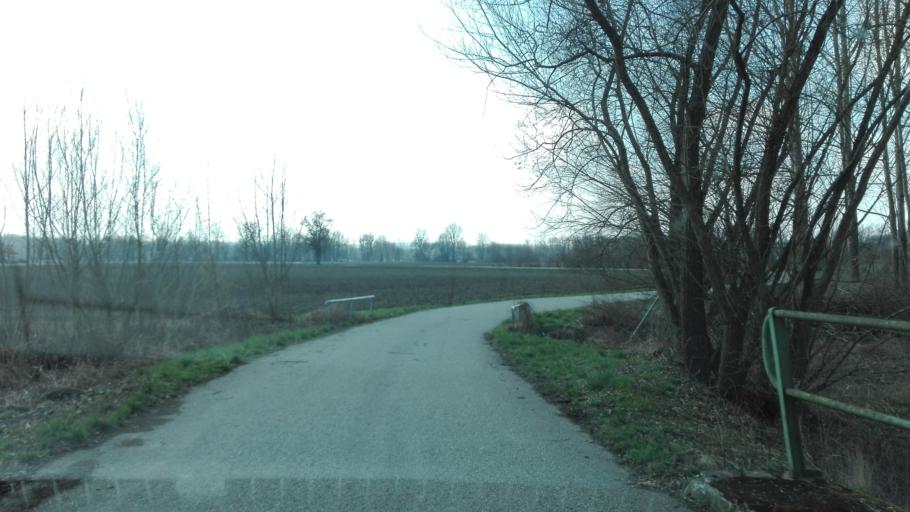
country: AT
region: Upper Austria
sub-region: Politischer Bezirk Urfahr-Umgebung
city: Goldworth
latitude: 48.3305
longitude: 14.0927
